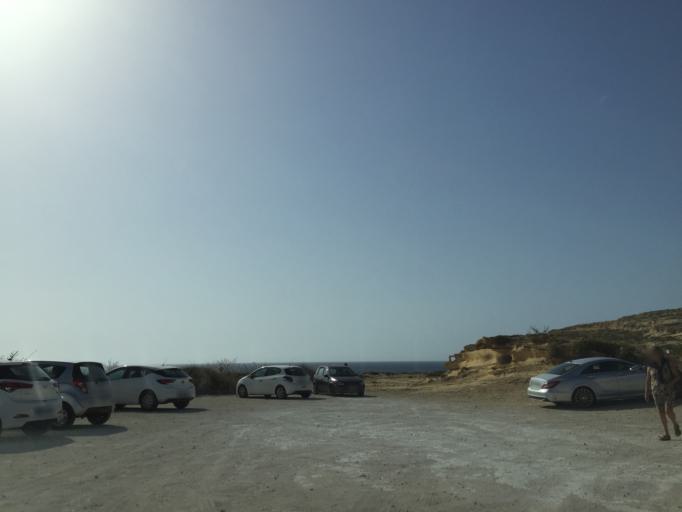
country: MT
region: Saint Lawrence
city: San Lawrenz
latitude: 36.0513
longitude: 14.1906
